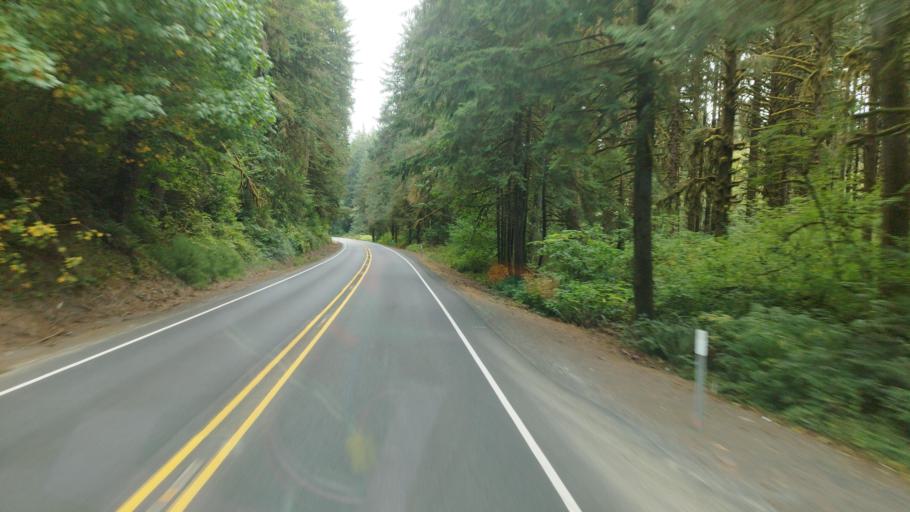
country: US
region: Oregon
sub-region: Clatsop County
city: Seaside
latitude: 45.8903
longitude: -123.6307
